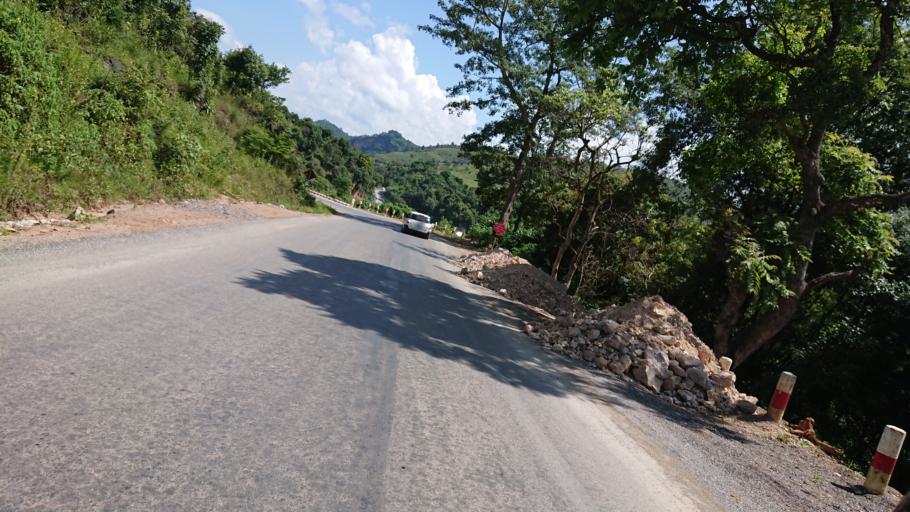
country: MM
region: Shan
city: Taunggyi
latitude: 20.8146
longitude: 97.3325
